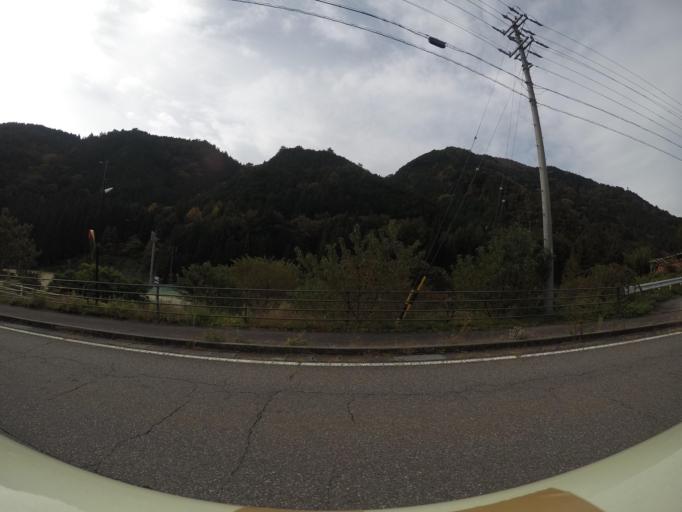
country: JP
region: Nagano
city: Ina
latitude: 35.8608
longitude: 137.6977
